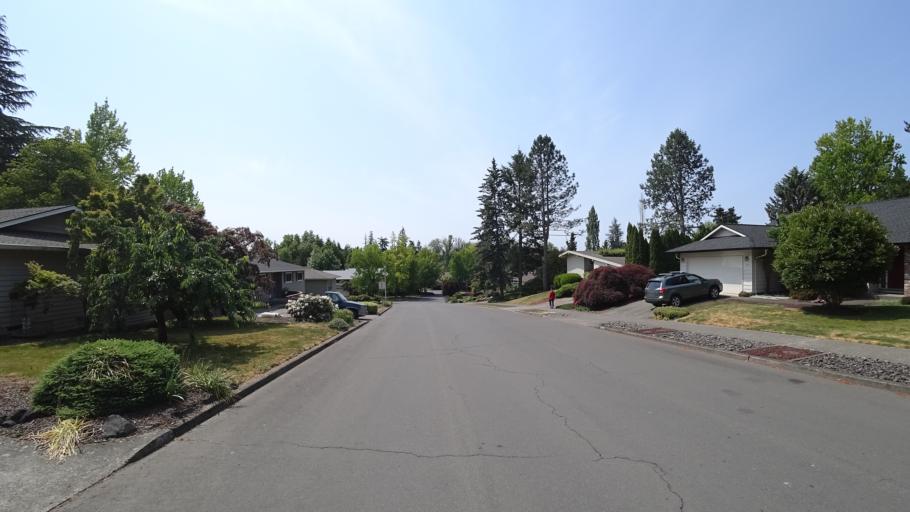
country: US
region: Oregon
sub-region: Washington County
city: Oak Hills
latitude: 45.5379
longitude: -122.8257
